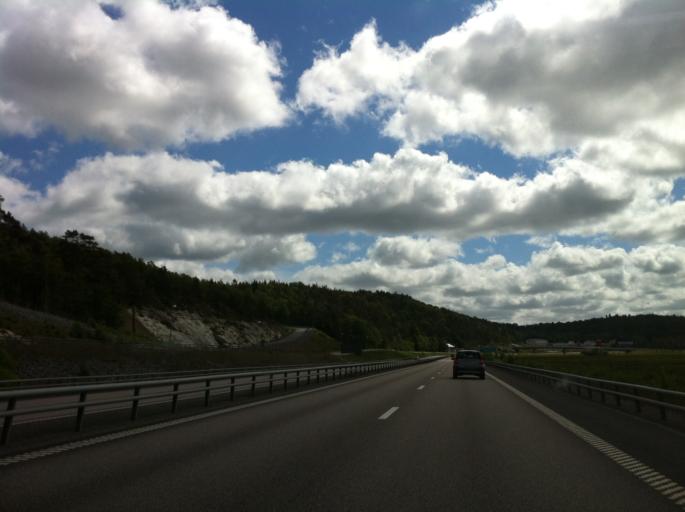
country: SE
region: Vaestra Goetaland
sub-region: Ale Kommun
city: Nodinge-Nol
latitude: 57.9083
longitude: 12.0518
